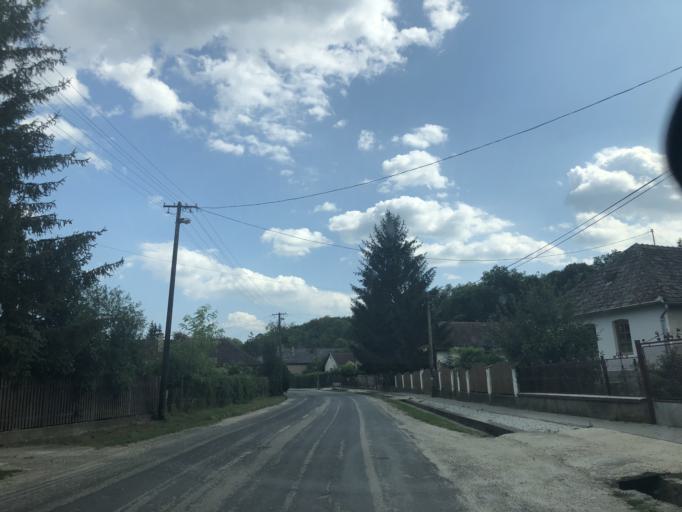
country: HU
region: Borsod-Abauj-Zemplen
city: Szendro
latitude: 48.4410
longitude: 20.7938
